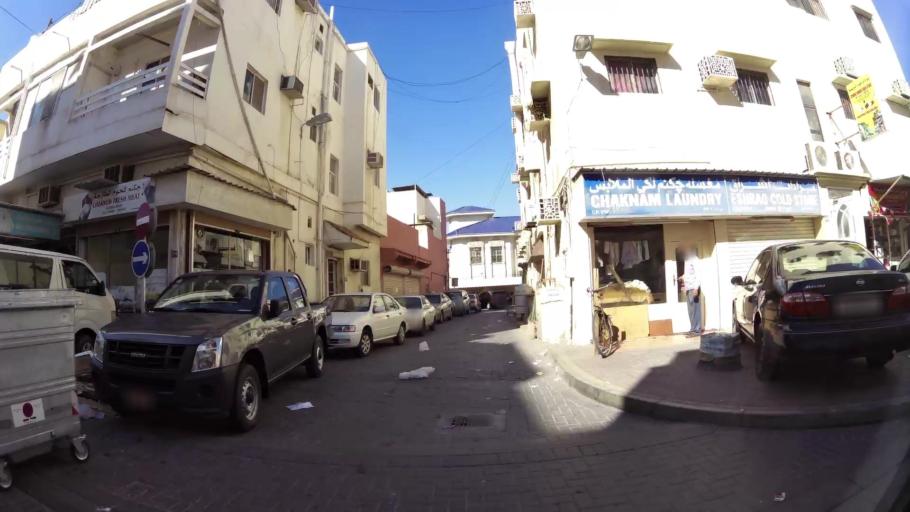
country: BH
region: Muharraq
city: Al Muharraq
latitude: 26.2600
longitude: 50.6122
